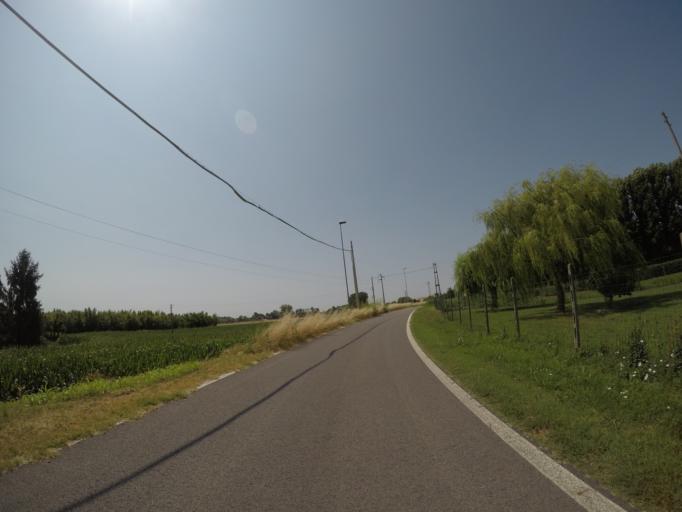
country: IT
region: Veneto
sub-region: Provincia di Rovigo
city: Fratta Polesine
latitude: 45.0122
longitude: 11.6425
